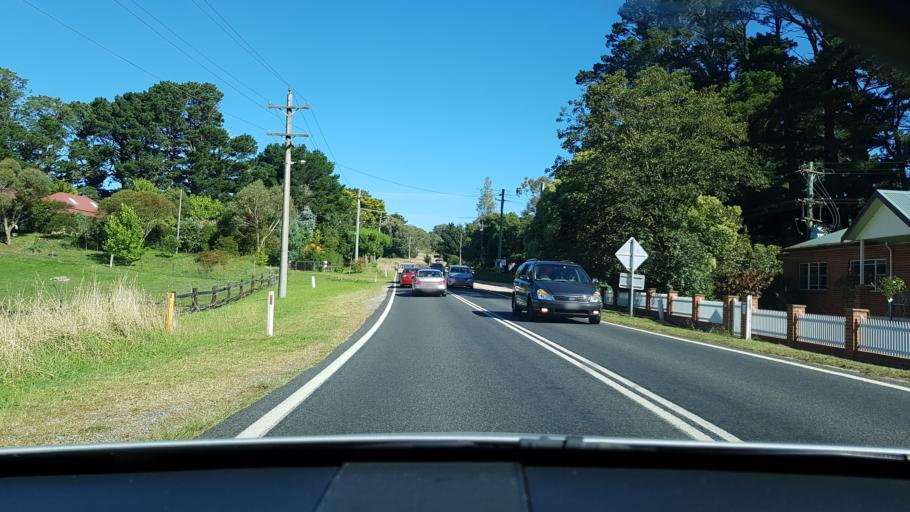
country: AU
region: New South Wales
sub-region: Lithgow
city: Bowenfels
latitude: -33.6446
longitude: 150.0478
